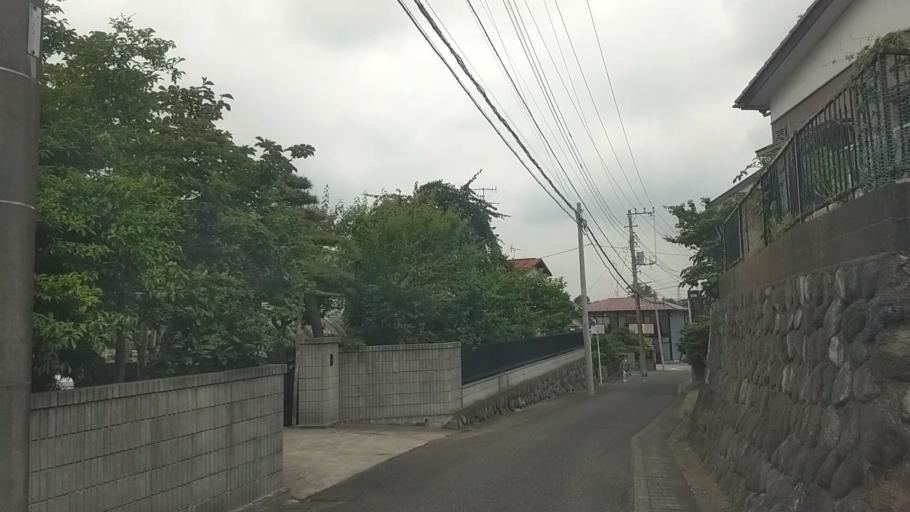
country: JP
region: Kanagawa
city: Kamakura
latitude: 35.3730
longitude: 139.5332
